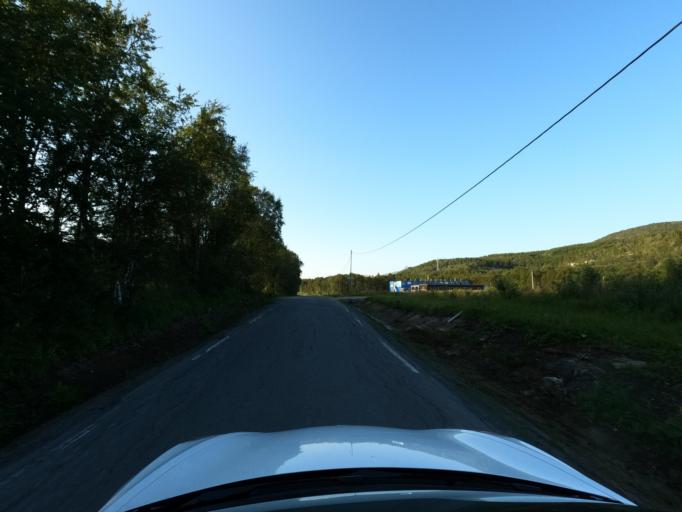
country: NO
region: Troms
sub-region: Skanland
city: Evenskjer
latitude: 68.4718
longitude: 16.7043
